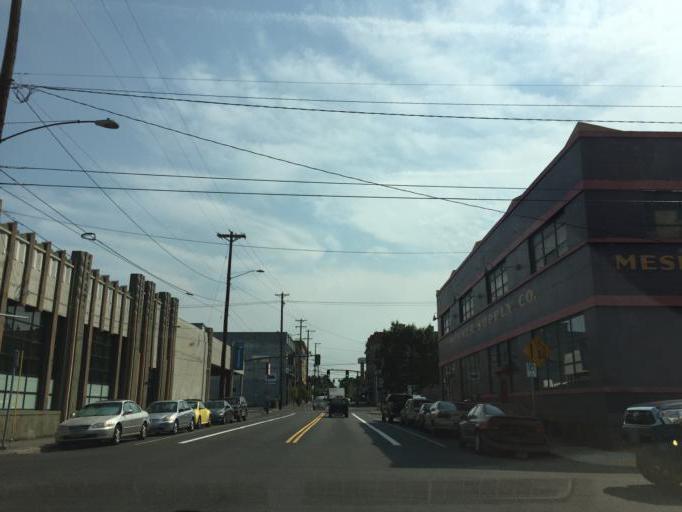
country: US
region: Oregon
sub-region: Multnomah County
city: Portland
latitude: 45.5194
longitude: -122.6629
